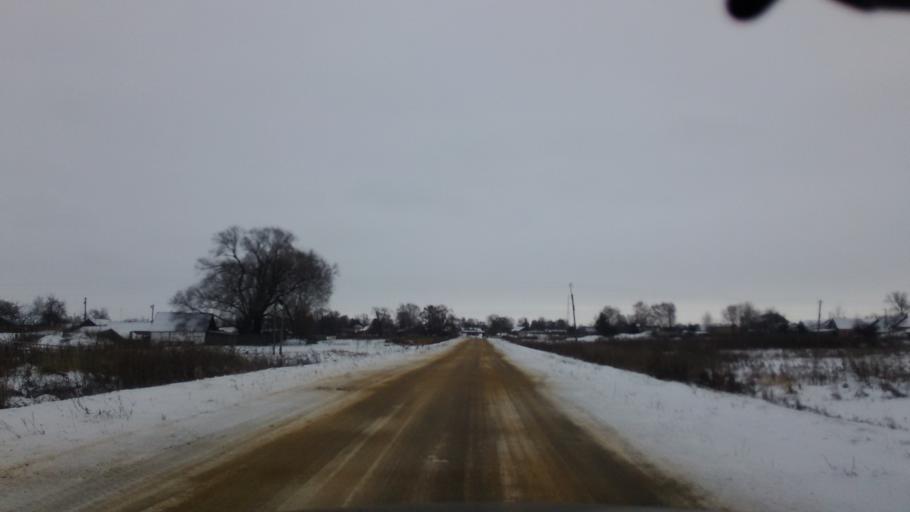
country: RU
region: Tula
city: Bogoroditsk
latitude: 53.7665
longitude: 37.9781
